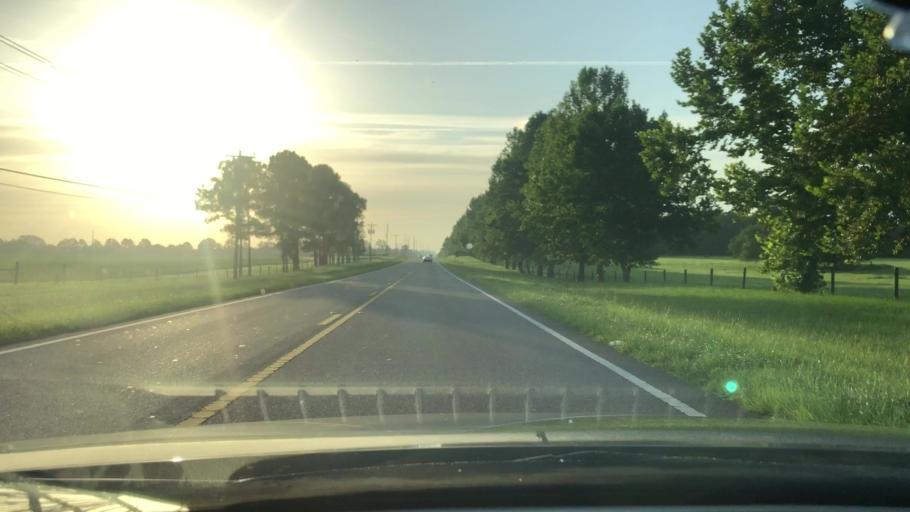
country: US
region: Florida
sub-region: Marion County
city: Belleview
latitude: 29.0261
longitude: -82.2101
